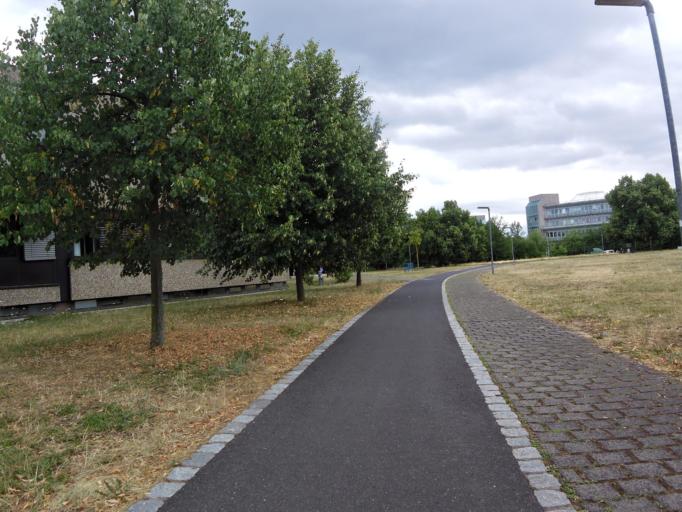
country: DE
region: Bavaria
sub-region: Regierungsbezirk Unterfranken
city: Wuerzburg
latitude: 49.7821
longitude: 9.9707
